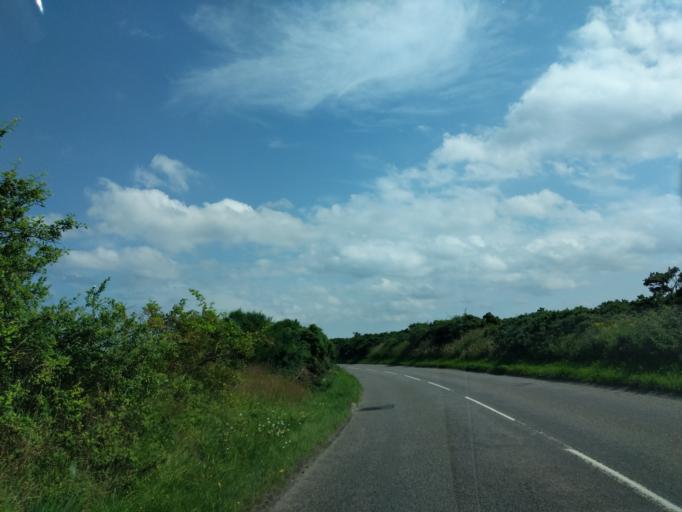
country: GB
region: Scotland
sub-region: Moray
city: Lossiemouth
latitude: 57.7171
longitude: -3.3165
